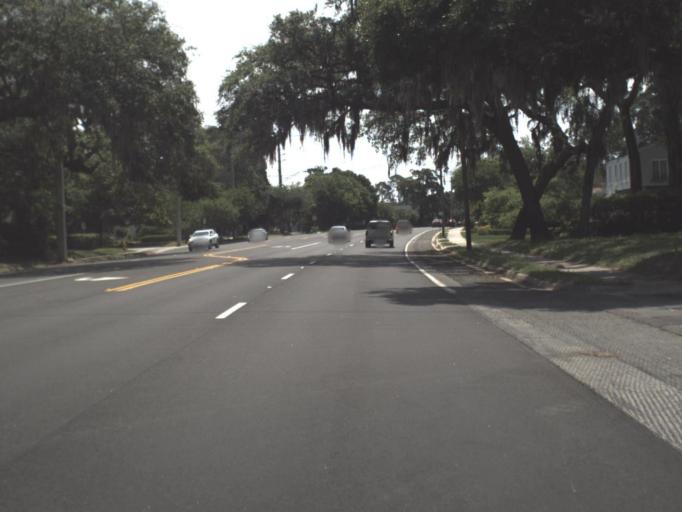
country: US
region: Florida
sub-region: Duval County
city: Jacksonville
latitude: 30.2458
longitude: -81.6301
